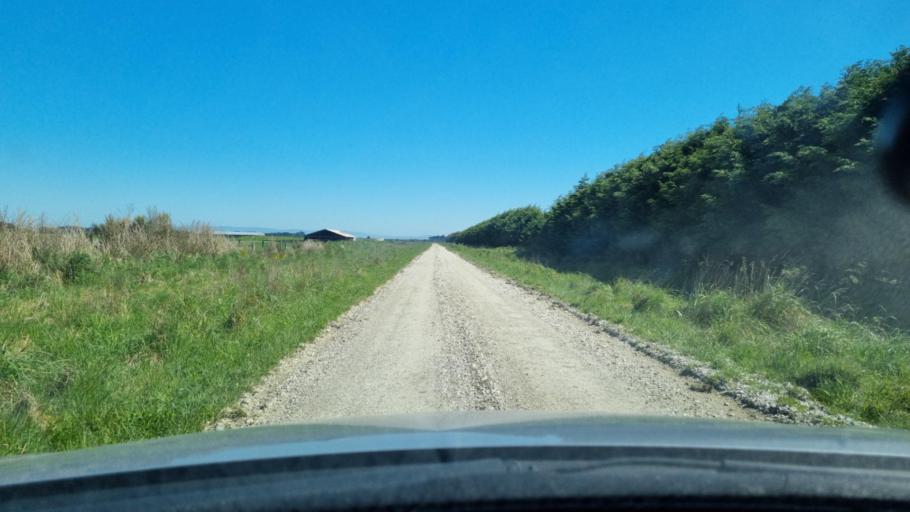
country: NZ
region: Southland
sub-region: Invercargill City
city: Invercargill
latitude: -46.4255
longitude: 168.3172
